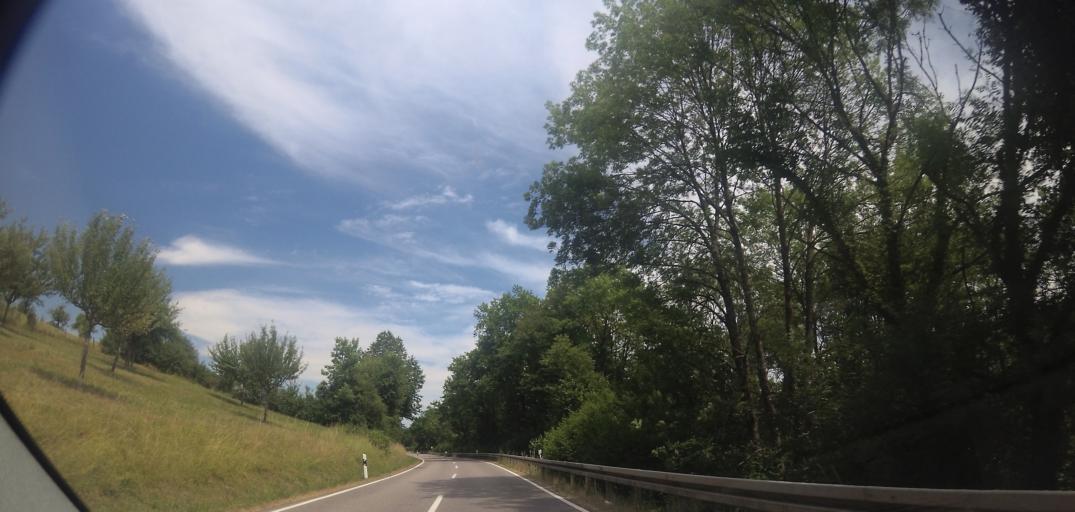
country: DE
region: Saarland
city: Merzig
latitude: 49.4177
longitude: 6.6046
